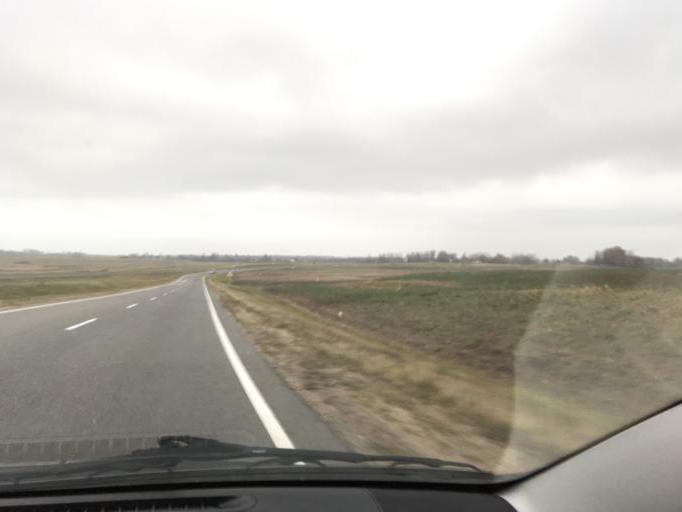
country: BY
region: Vitebsk
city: Vitebsk
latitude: 55.1575
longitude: 30.0649
